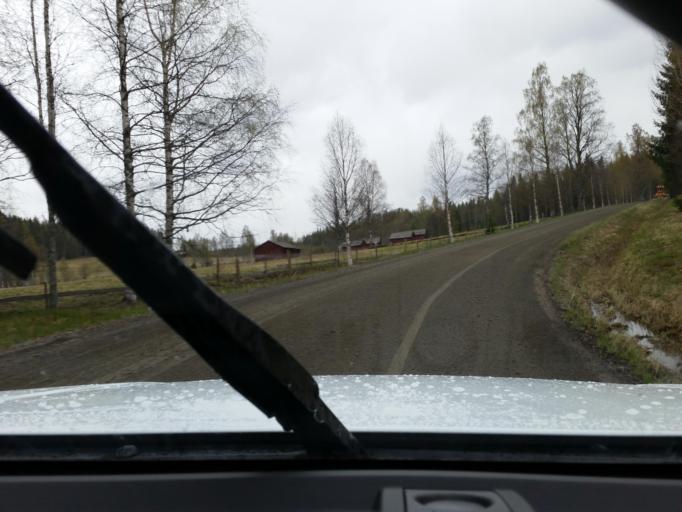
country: SE
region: Norrbotten
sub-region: Pitea Kommun
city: Norrfjarden
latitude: 65.5734
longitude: 21.4856
